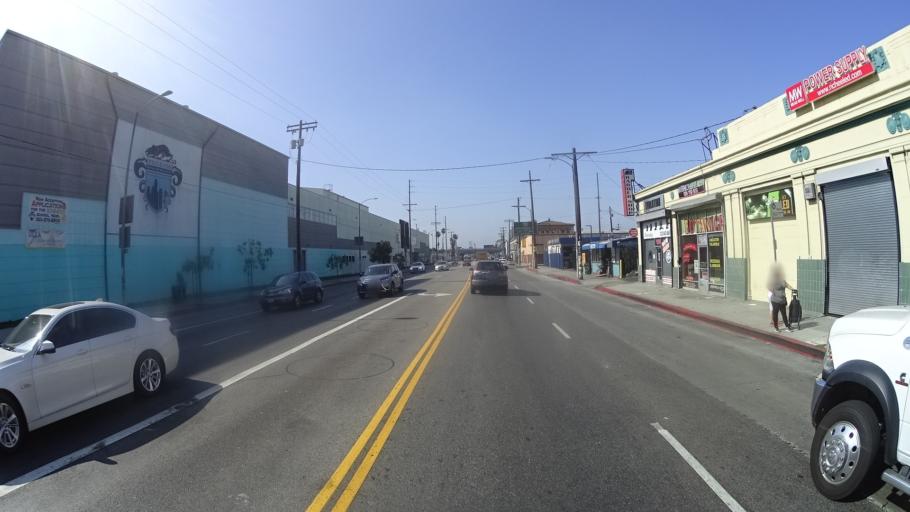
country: US
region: California
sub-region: Los Angeles County
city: Echo Park
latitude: 34.0399
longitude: -118.2917
